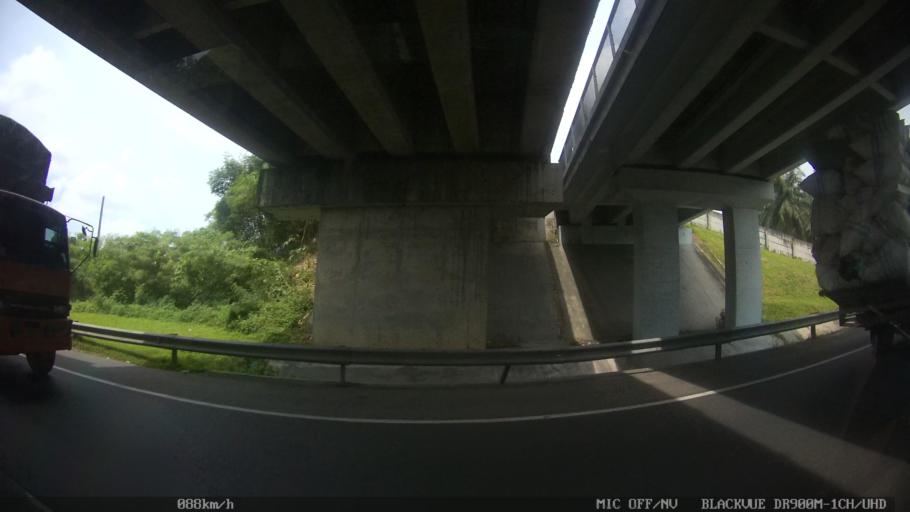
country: ID
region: North Sumatra
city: Labuhan Deli
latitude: 3.6719
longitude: 98.6805
